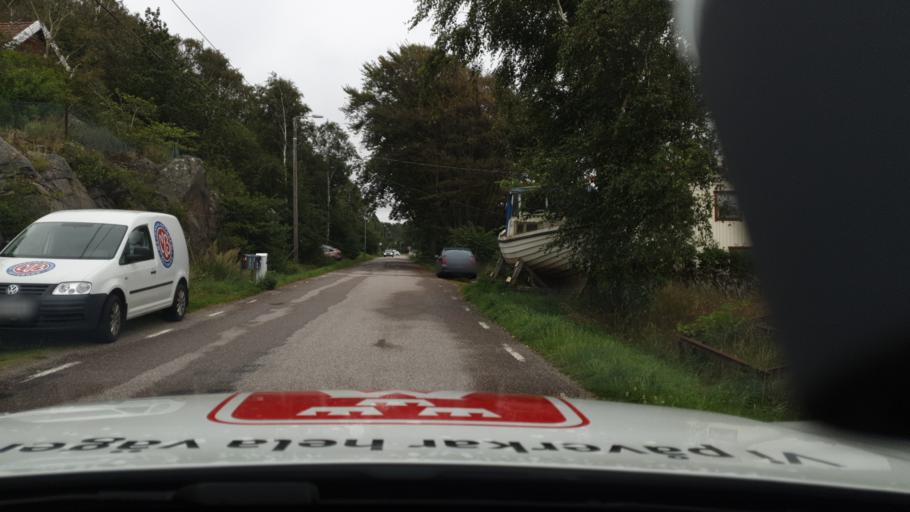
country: SE
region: Vaestra Goetaland
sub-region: Kungalvs Kommun
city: Kode
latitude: 57.8990
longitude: 11.7249
